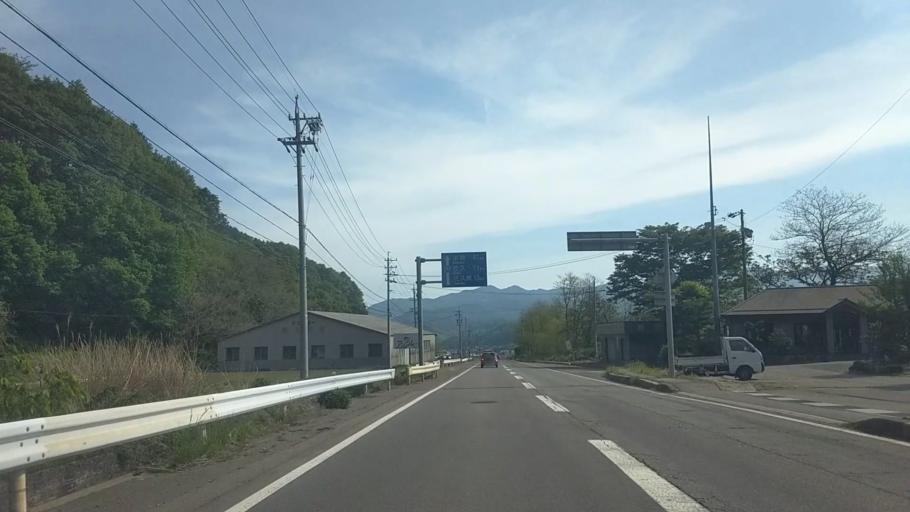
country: JP
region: Nagano
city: Saku
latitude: 36.0630
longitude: 138.4706
